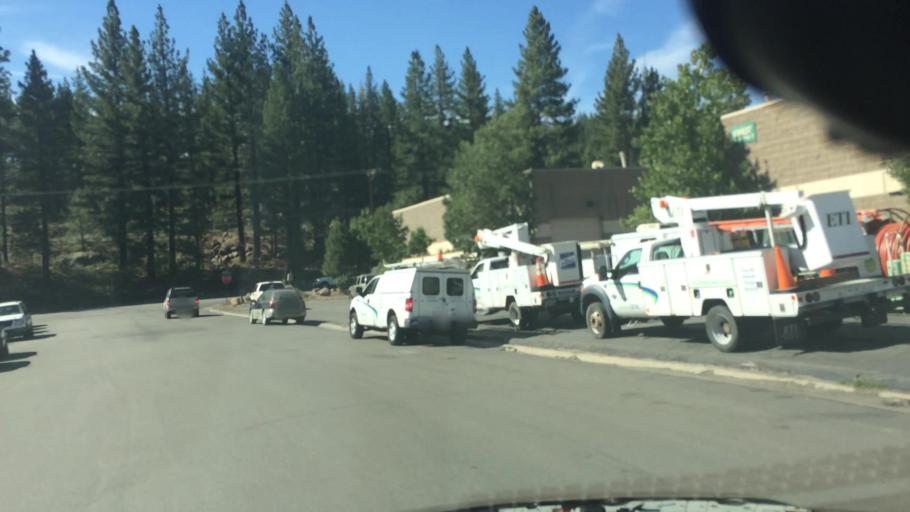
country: US
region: California
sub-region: Nevada County
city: Truckee
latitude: 39.3225
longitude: -120.1930
